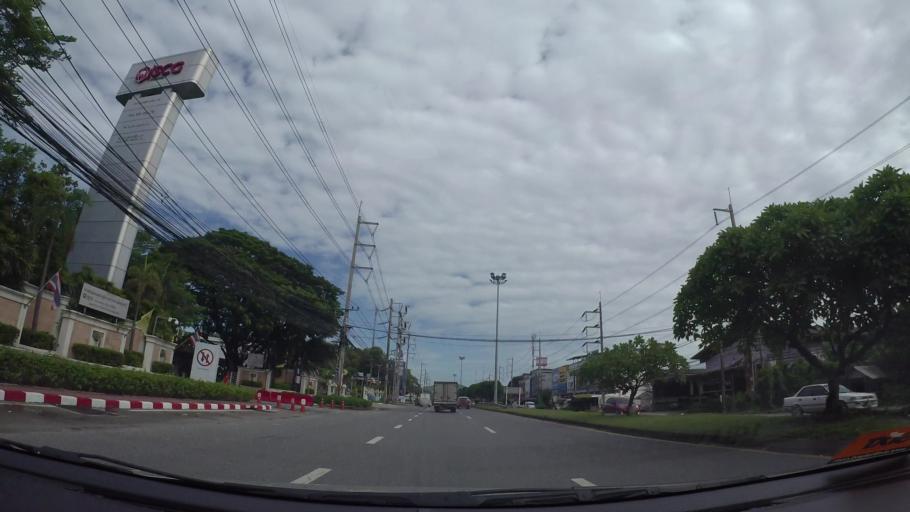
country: TH
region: Rayong
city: Ban Chang
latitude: 12.7223
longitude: 101.1530
